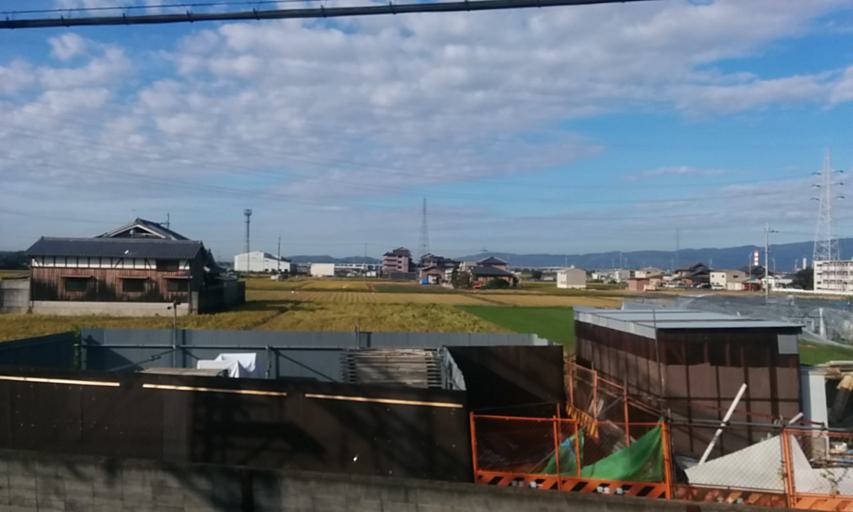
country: JP
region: Kyoto
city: Uji
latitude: 34.9176
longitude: 135.7683
